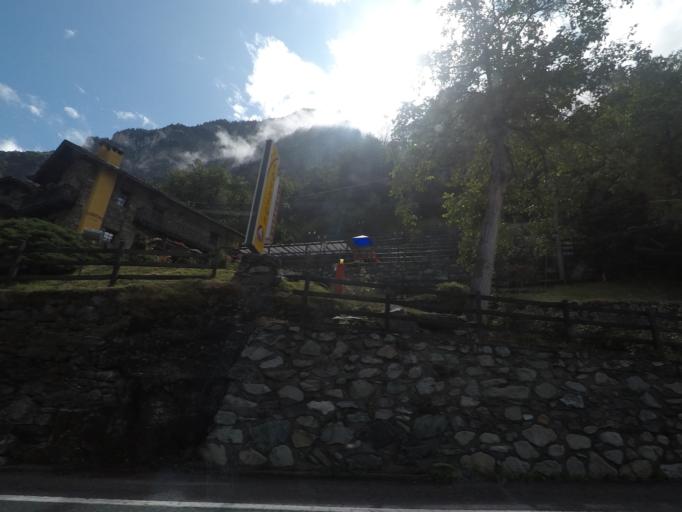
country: IT
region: Aosta Valley
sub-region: Valle d'Aosta
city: Antey-Saint-Andre
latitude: 45.7760
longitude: 7.5929
